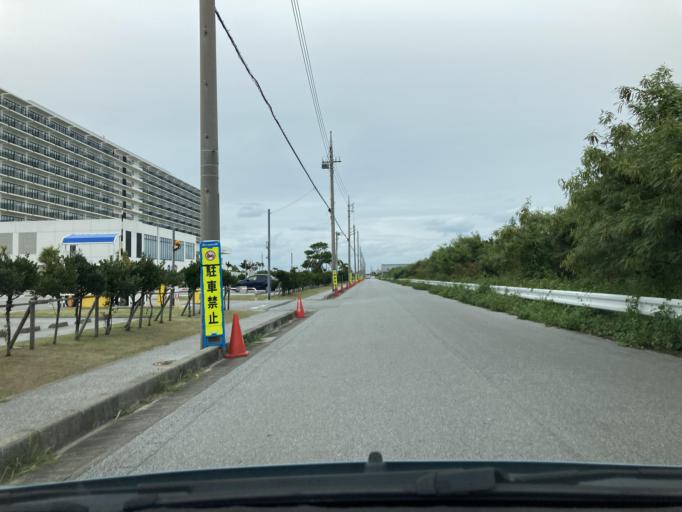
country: JP
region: Okinawa
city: Itoman
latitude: 26.1308
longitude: 127.6541
